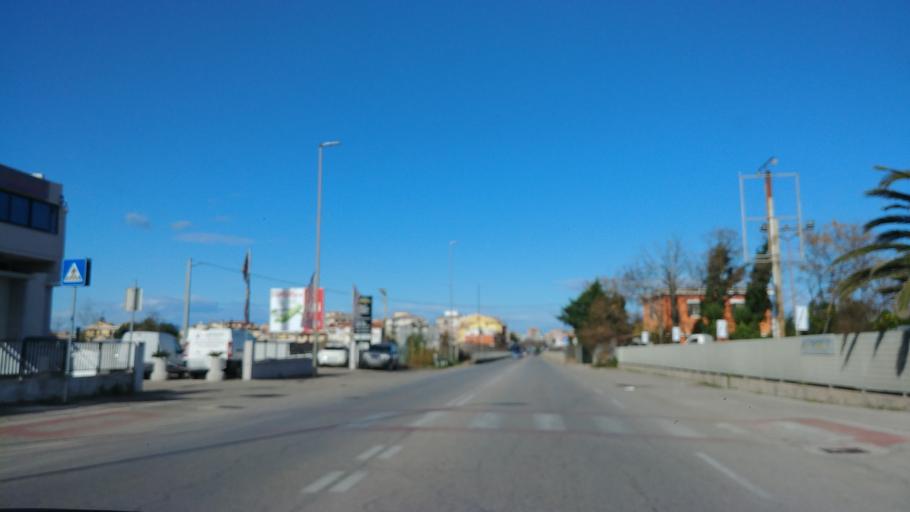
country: IT
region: Molise
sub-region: Provincia di Campobasso
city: Termoli
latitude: 41.9891
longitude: 15.0014
